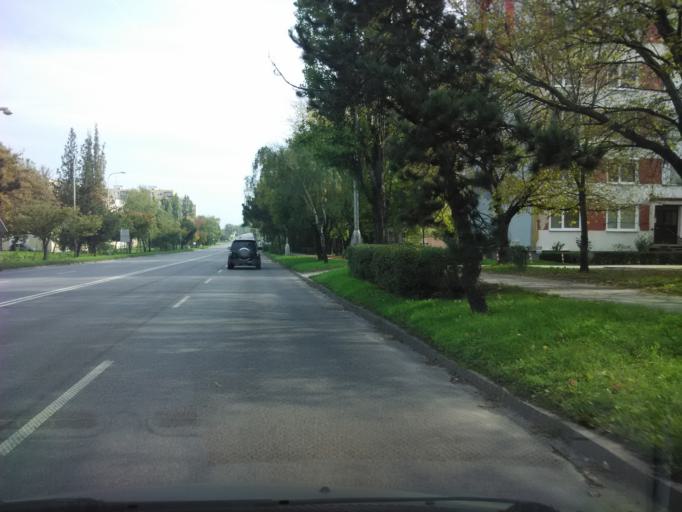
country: SK
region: Nitriansky
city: Komarno
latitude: 47.7626
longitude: 18.1334
